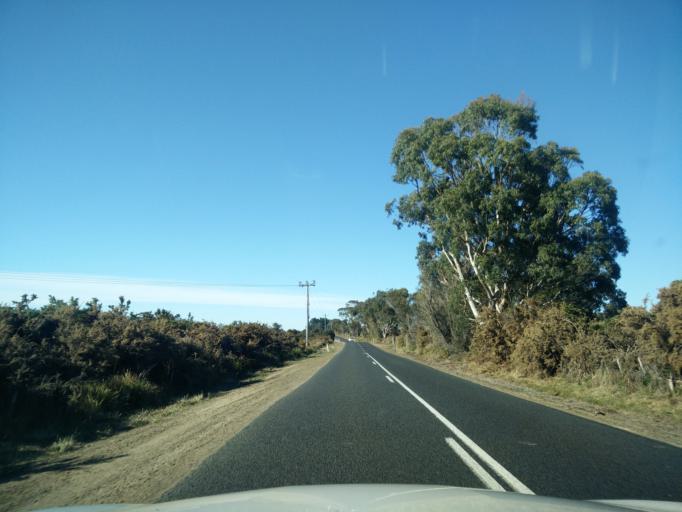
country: AU
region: Tasmania
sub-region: Break O'Day
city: St Helens
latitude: -41.9285
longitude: 148.2291
